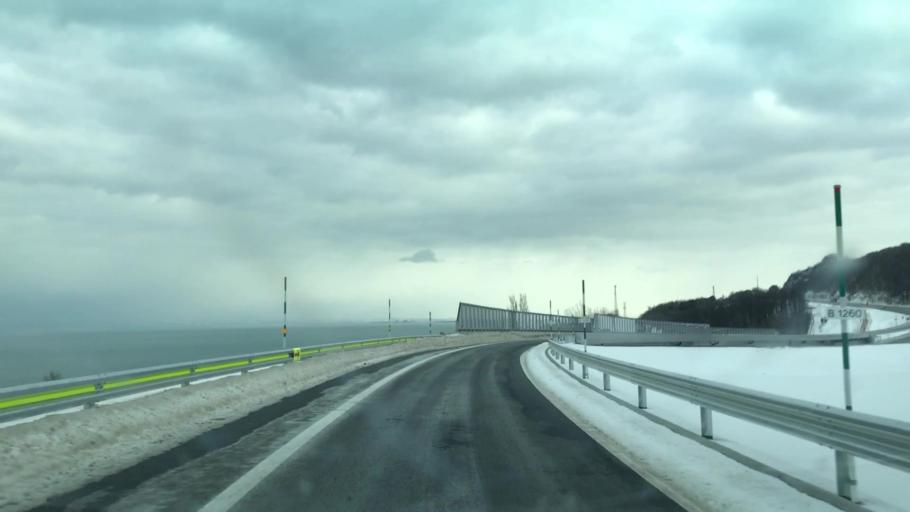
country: JP
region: Hokkaido
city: Otaru
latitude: 43.1706
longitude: 141.0690
